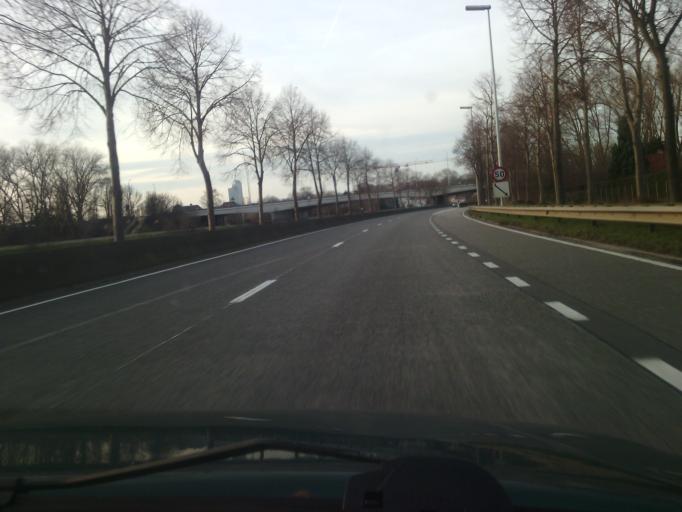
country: BE
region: Flanders
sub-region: Provincie Oost-Vlaanderen
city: Gent
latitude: 51.0158
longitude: 3.7122
